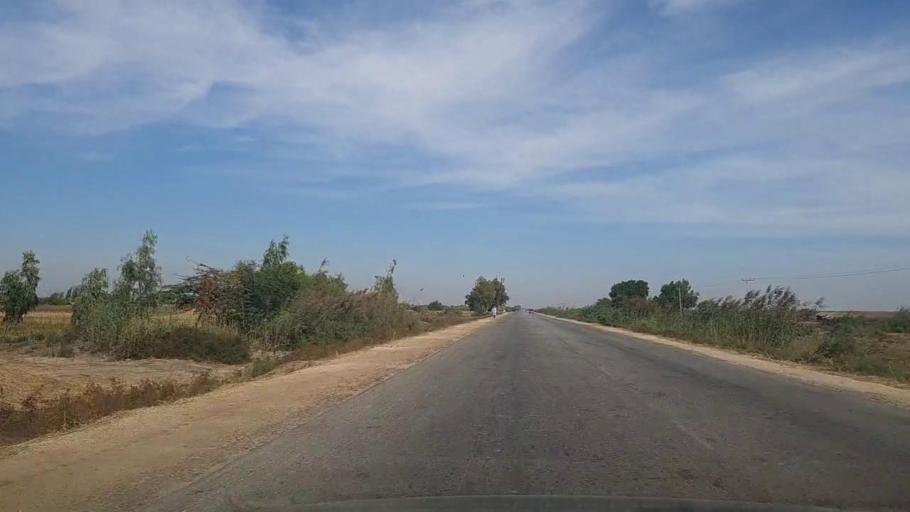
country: PK
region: Sindh
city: Daro Mehar
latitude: 24.9392
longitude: 68.1085
